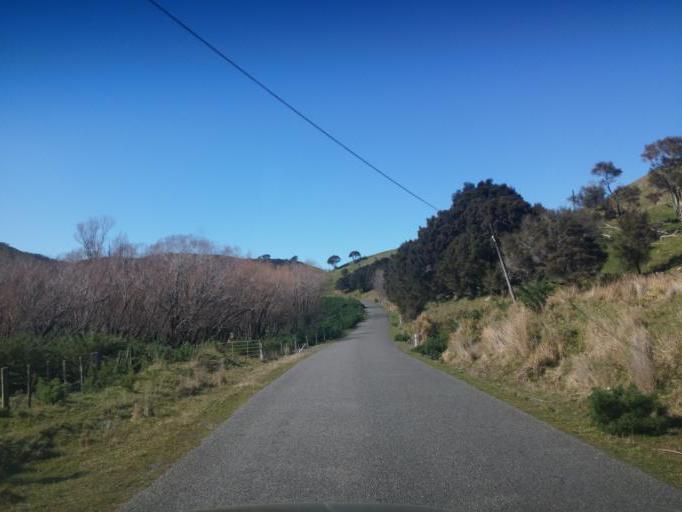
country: NZ
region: Wellington
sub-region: South Wairarapa District
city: Waipawa
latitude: -41.4204
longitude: 175.4955
